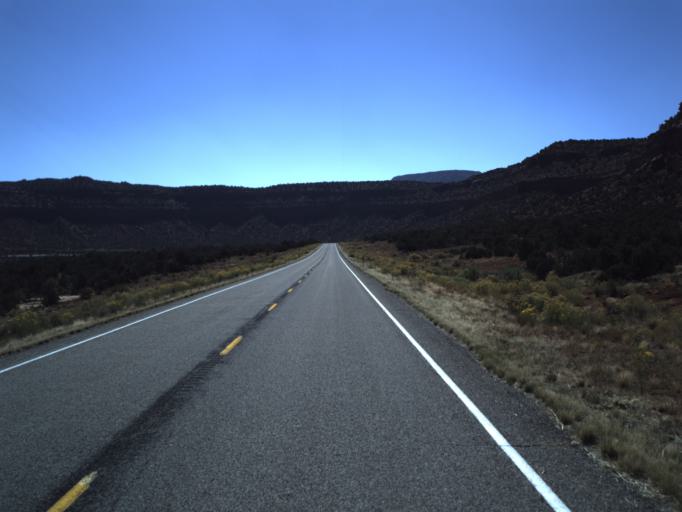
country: US
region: Utah
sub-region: San Juan County
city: Blanding
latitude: 37.6187
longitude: -110.0838
